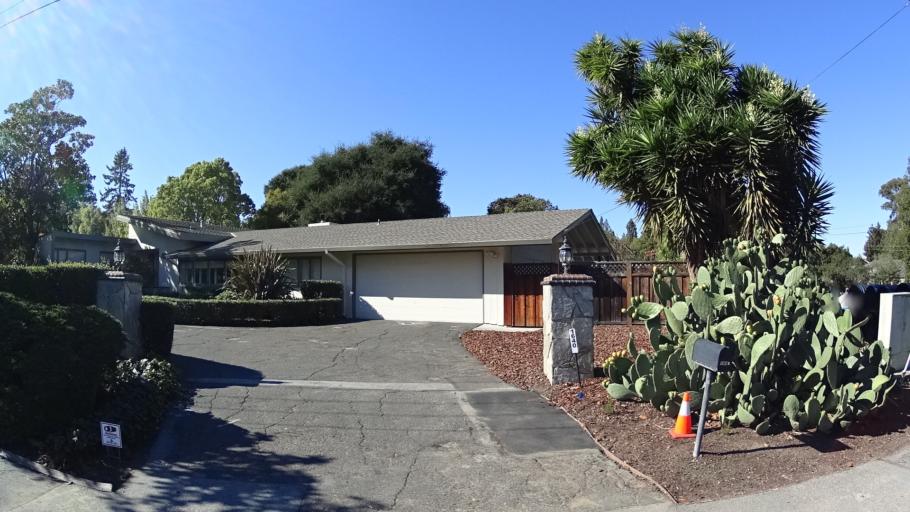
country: US
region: California
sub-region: San Mateo County
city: Burlingame
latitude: 37.5768
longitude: -122.3561
